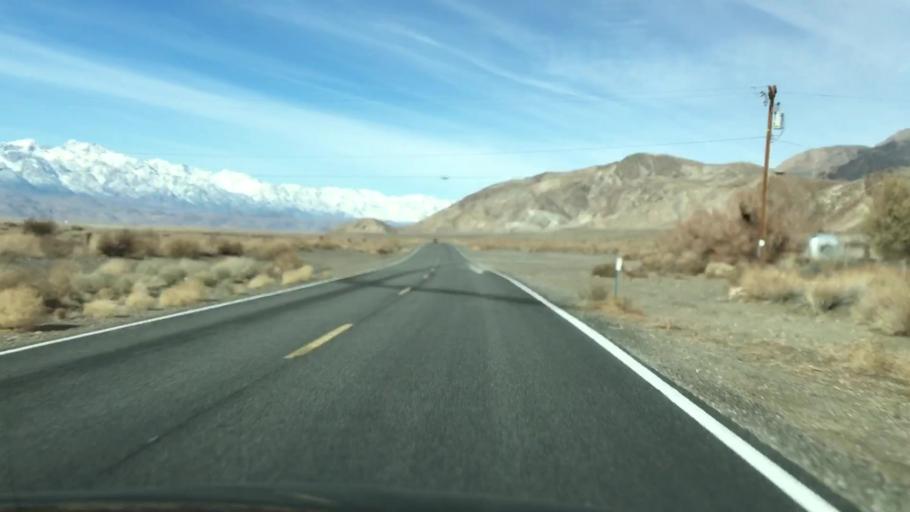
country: US
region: California
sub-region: Inyo County
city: Lone Pine
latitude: 36.5239
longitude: -117.9044
